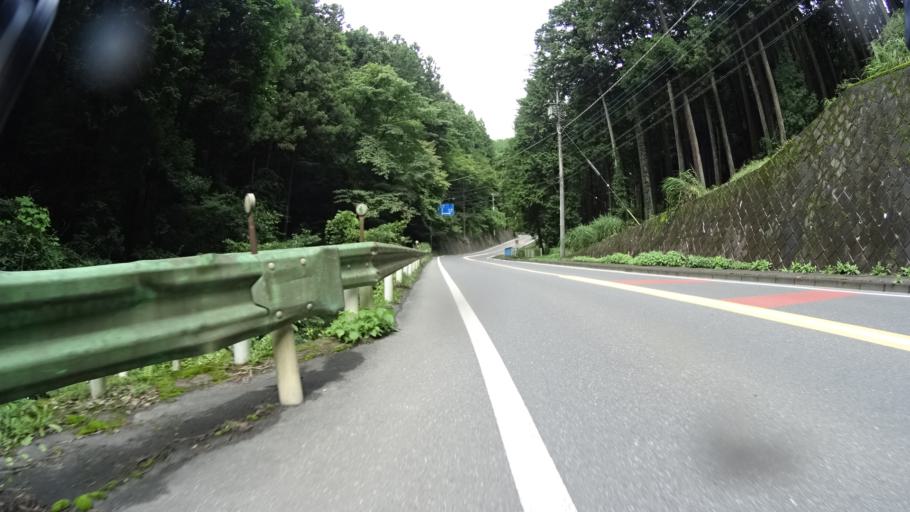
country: JP
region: Tokyo
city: Ome
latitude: 35.8270
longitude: 139.2187
